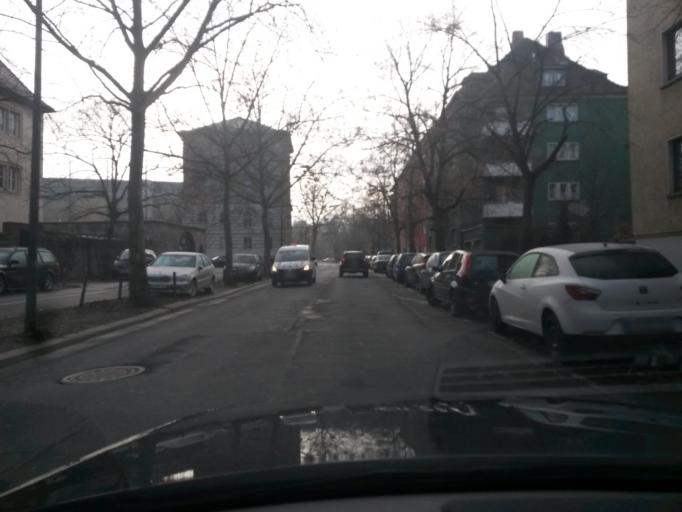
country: DE
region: Bavaria
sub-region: Regierungsbezirk Unterfranken
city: Wuerzburg
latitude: 49.7899
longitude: 9.9359
